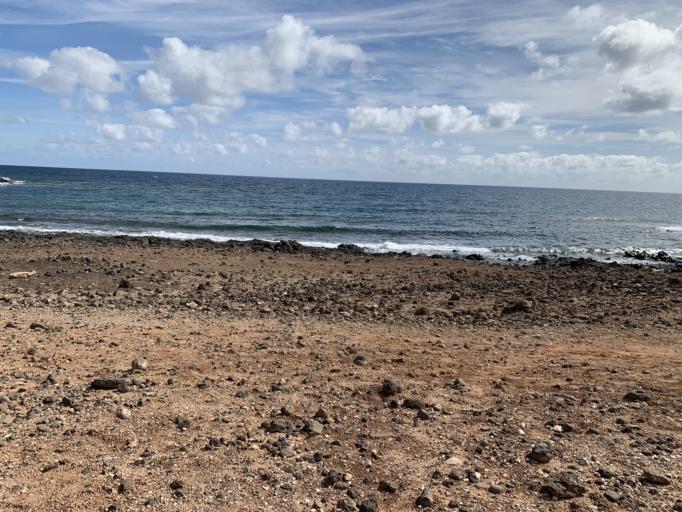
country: ES
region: Canary Islands
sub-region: Provincia de Las Palmas
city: Puerto del Rosario
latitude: 28.5013
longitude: -13.8474
